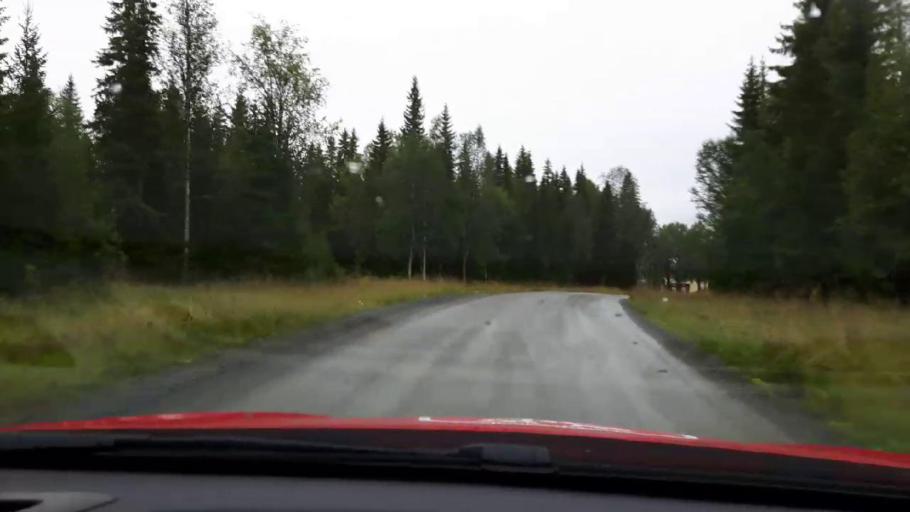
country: SE
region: Jaemtland
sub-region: Are Kommun
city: Are
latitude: 63.4310
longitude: 12.8024
